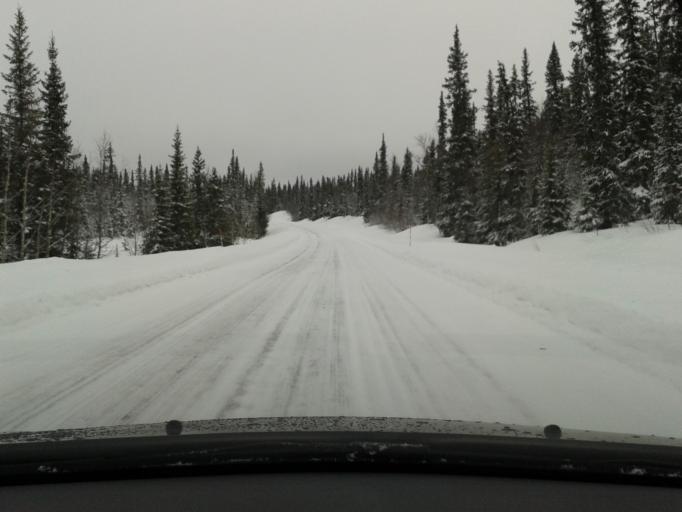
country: SE
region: Vaesterbotten
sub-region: Vilhelmina Kommun
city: Sjoberg
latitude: 65.1317
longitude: 15.8761
